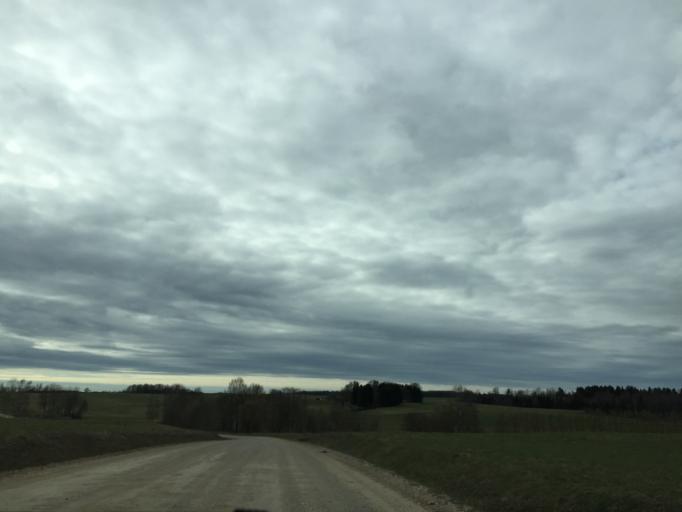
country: LT
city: Silale
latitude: 55.6186
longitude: 22.1956
